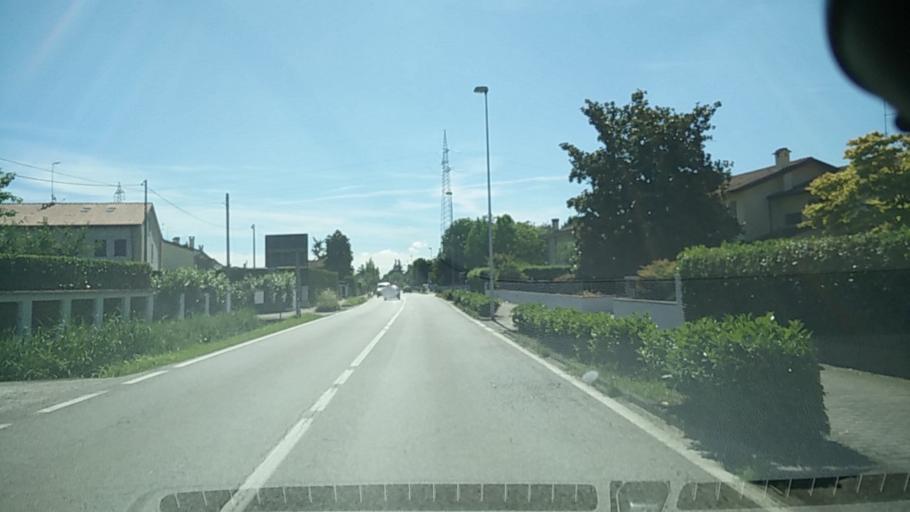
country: IT
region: Veneto
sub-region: Provincia di Venezia
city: Scorze
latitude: 45.5758
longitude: 12.1004
